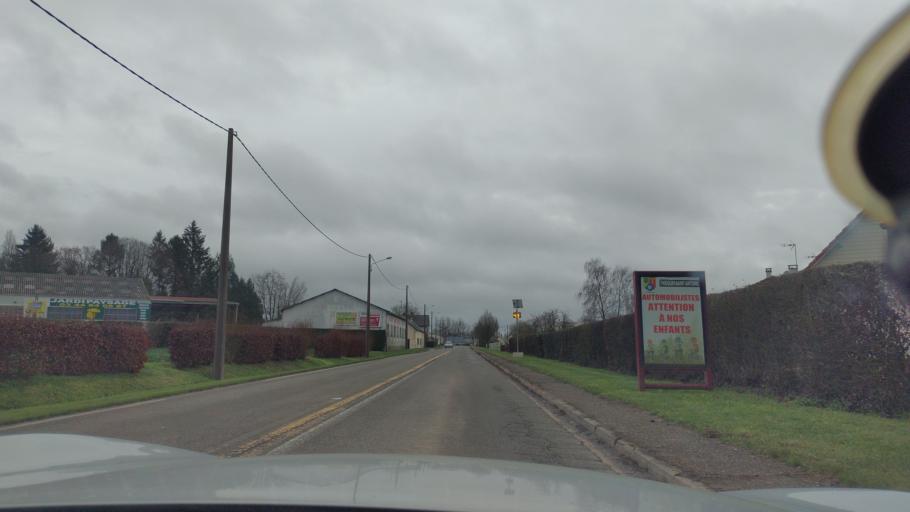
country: FR
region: Picardie
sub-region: Departement de l'Oise
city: Grandvilliers
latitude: 49.6373
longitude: 1.9460
